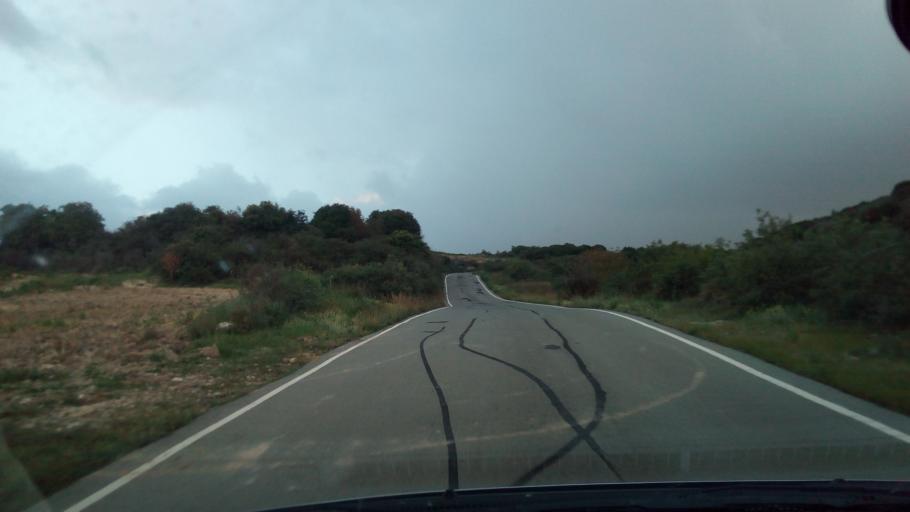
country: CY
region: Pafos
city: Polis
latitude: 34.9642
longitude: 32.4425
